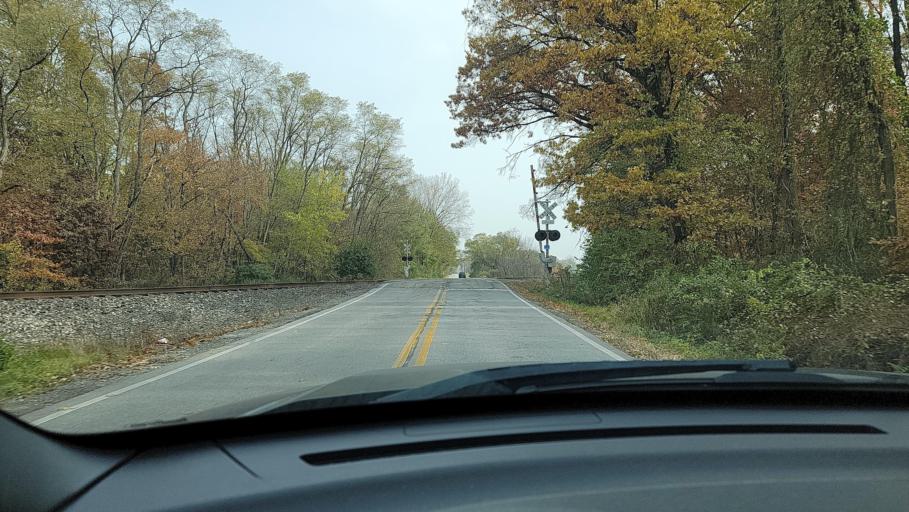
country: US
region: Indiana
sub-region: Porter County
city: Portage
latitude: 41.5867
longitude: -87.1802
